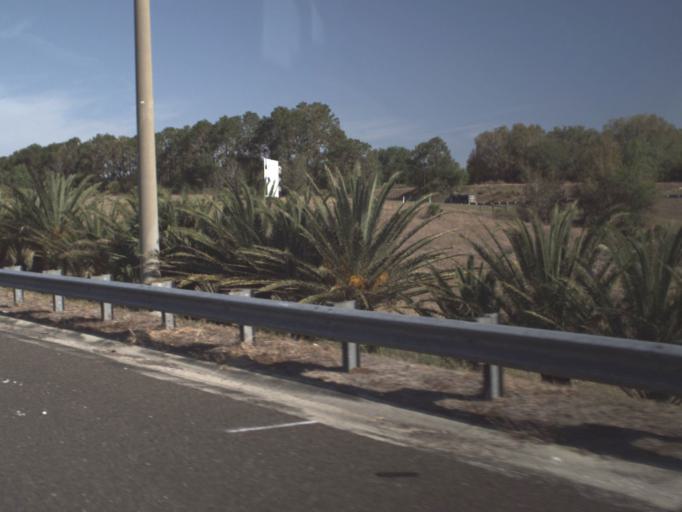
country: US
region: Florida
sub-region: Lake County
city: Minneola
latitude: 28.6333
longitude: -81.7770
